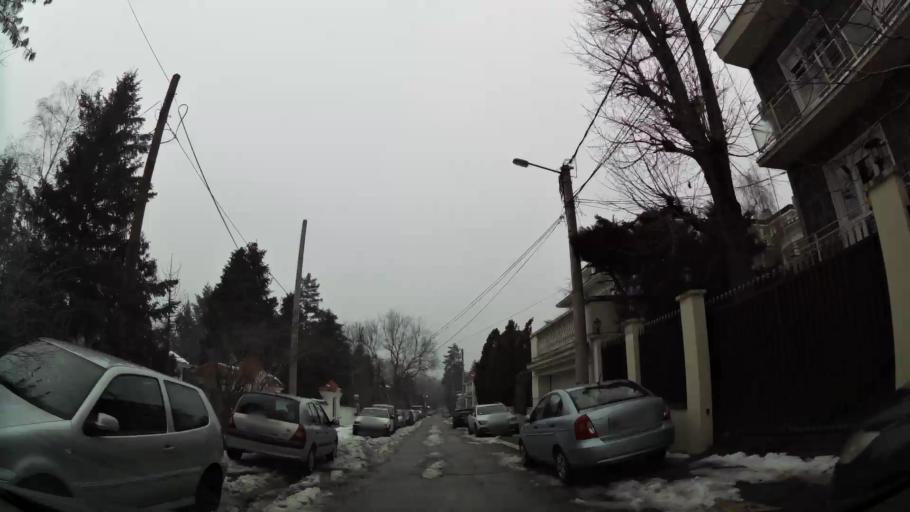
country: RS
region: Central Serbia
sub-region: Belgrade
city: Savski Venac
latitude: 44.7835
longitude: 20.4467
